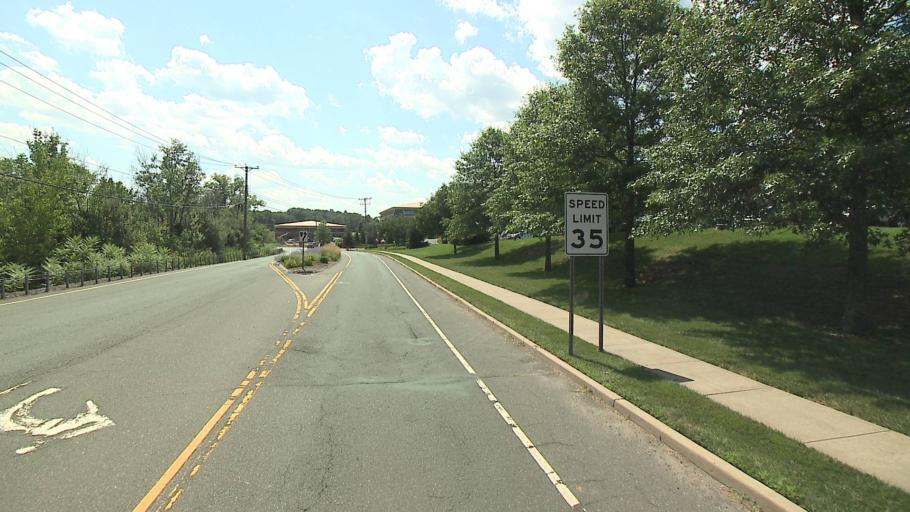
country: US
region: Connecticut
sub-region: Hartford County
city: Farmington
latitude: 41.7262
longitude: -72.8022
